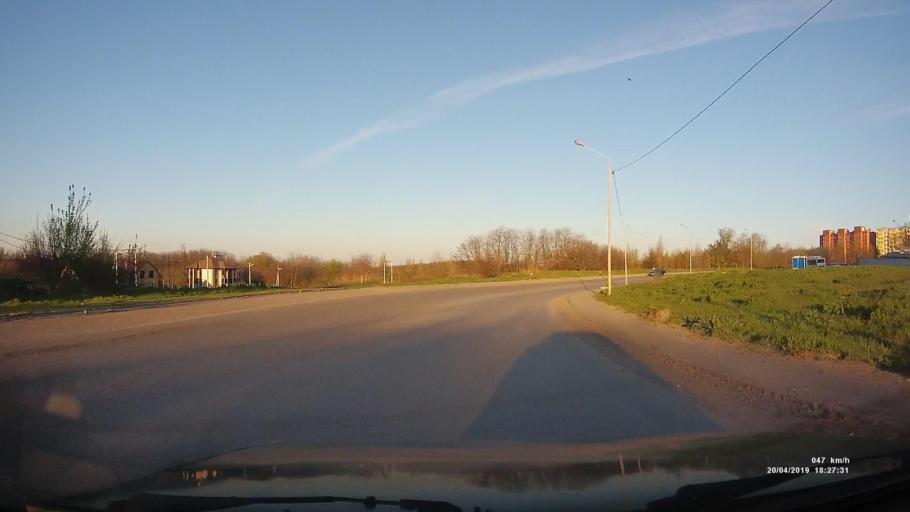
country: RU
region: Rostov
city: Aksay
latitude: 47.2457
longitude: 39.8313
